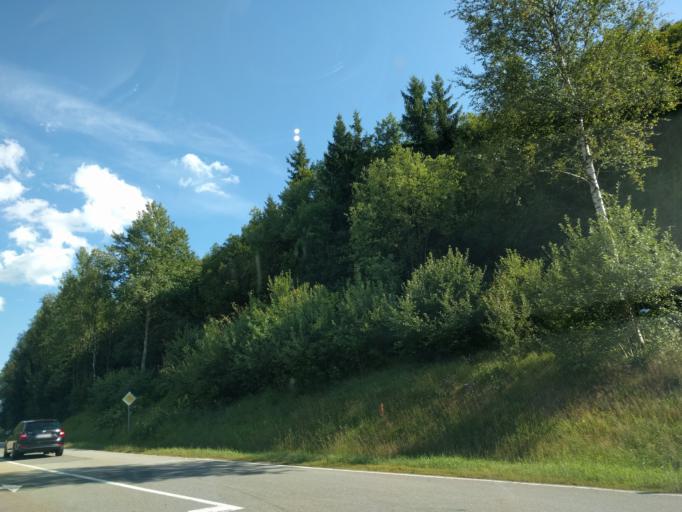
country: DE
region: Bavaria
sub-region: Lower Bavaria
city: Bodenmais
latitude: 49.0516
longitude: 13.1088
